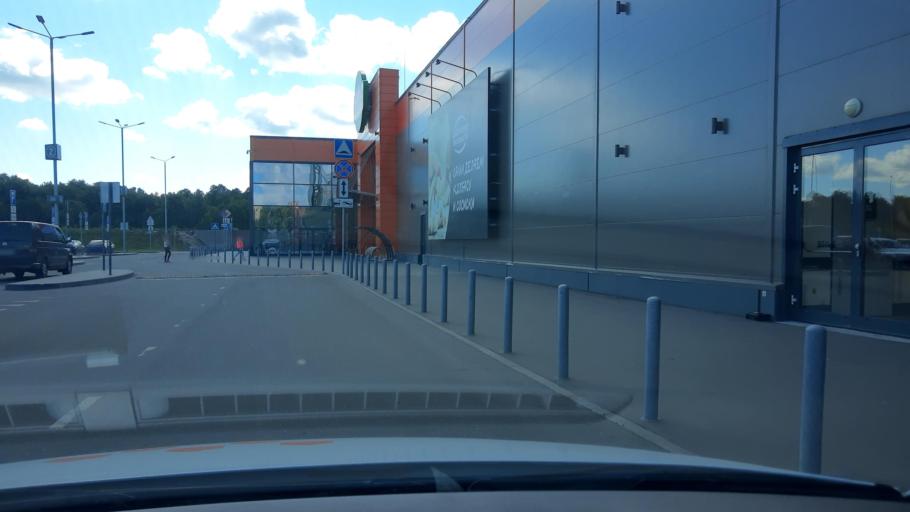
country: RU
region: Moskovskaya
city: Balashikha
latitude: 55.7927
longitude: 37.9456
